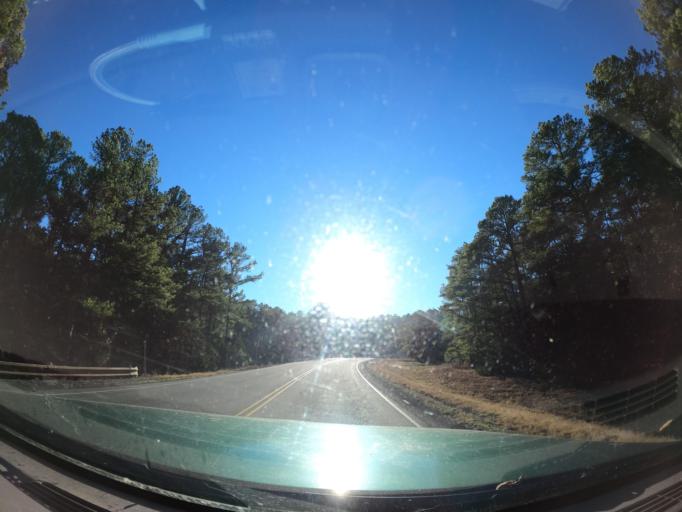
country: US
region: Oklahoma
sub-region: Latimer County
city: Wilburton
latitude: 35.0018
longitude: -95.3345
